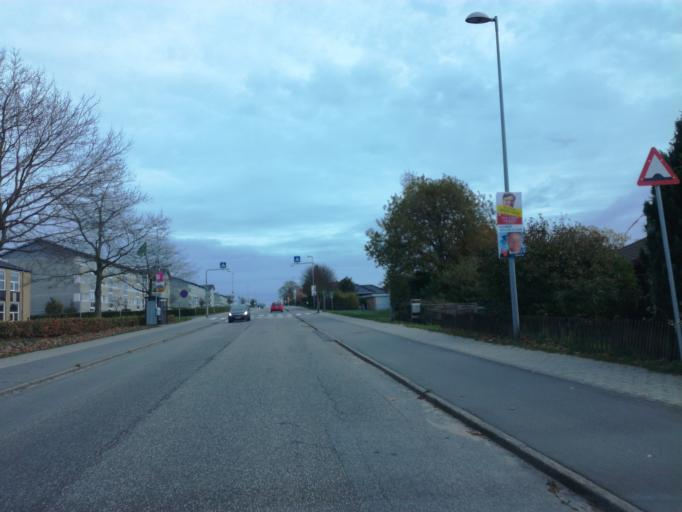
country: DK
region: South Denmark
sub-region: Fredericia Kommune
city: Fredericia
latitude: 55.5783
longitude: 9.7706
